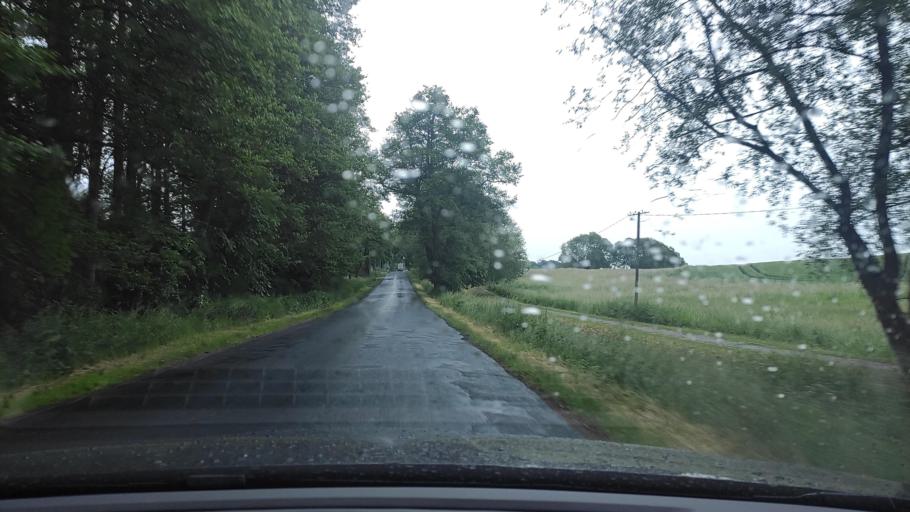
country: PL
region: Greater Poland Voivodeship
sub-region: Powiat poznanski
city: Kobylnica
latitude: 52.4890
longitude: 17.0925
